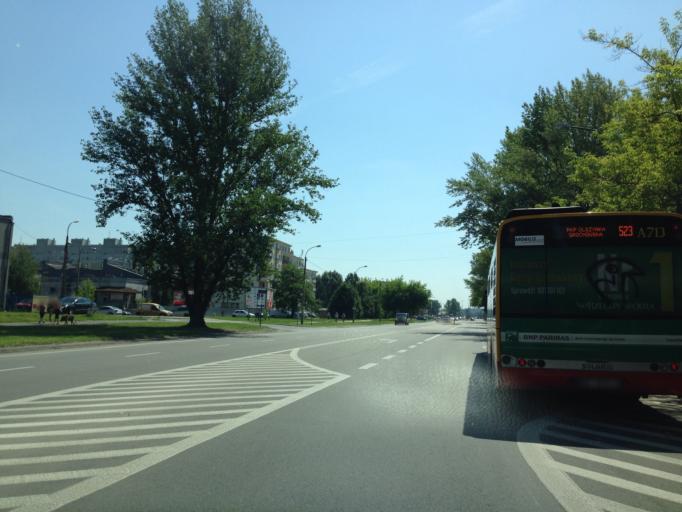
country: PL
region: Masovian Voivodeship
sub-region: Warszawa
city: Bemowo
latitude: 52.2544
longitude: 20.9086
